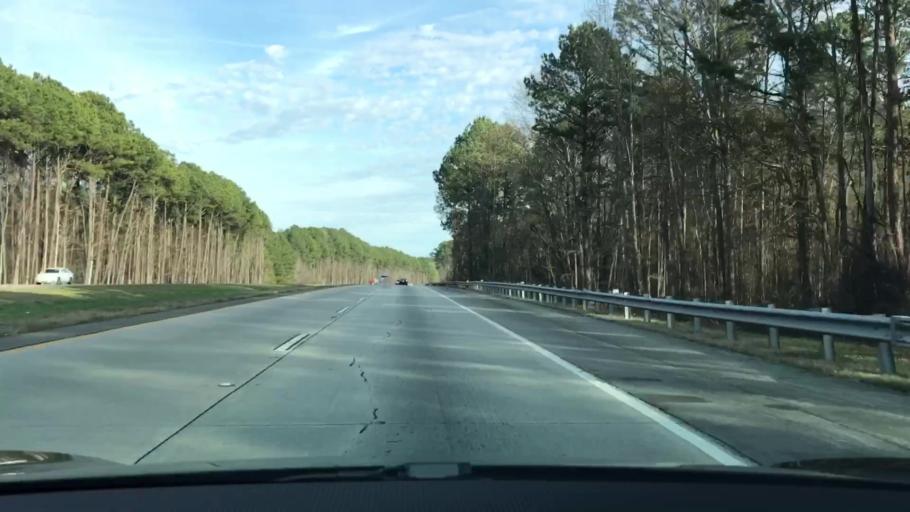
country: US
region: Georgia
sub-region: Greene County
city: Greensboro
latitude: 33.5492
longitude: -83.1380
